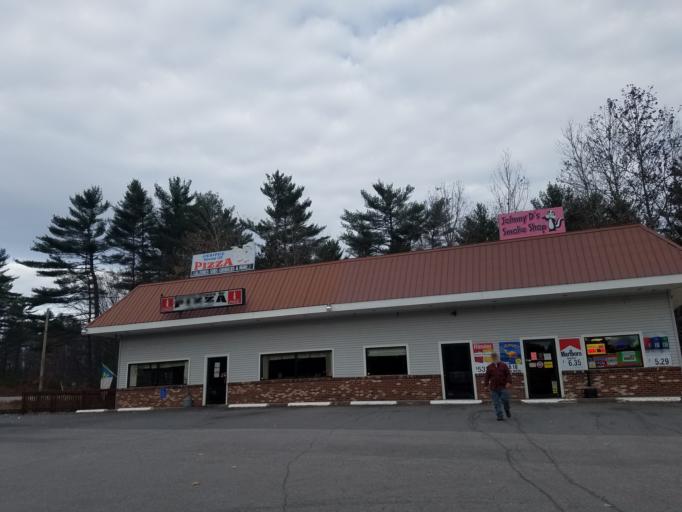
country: US
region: New Hampshire
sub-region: Carroll County
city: Ossipee
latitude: 43.6860
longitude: -71.0896
